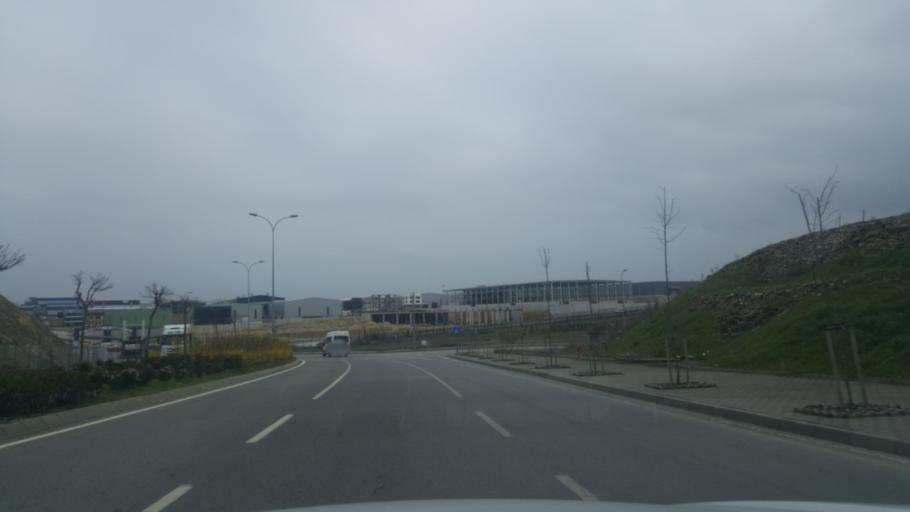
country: TR
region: Kocaeli
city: Tavsanli
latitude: 40.8293
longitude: 29.5589
